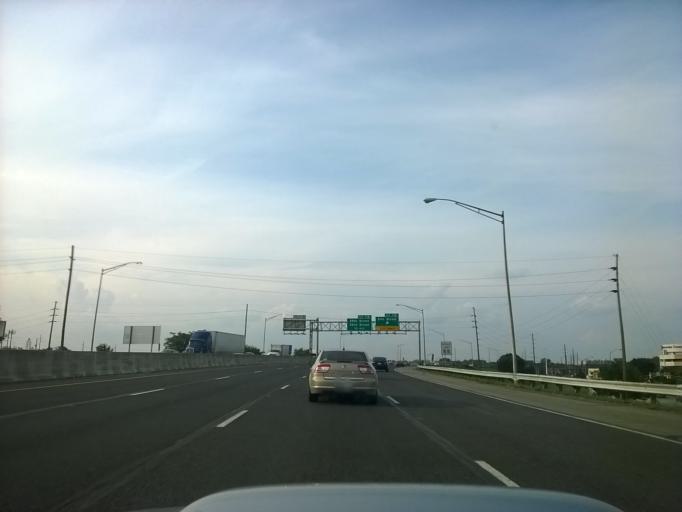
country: US
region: Indiana
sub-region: Marion County
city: Indianapolis
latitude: 39.7892
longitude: -86.1663
